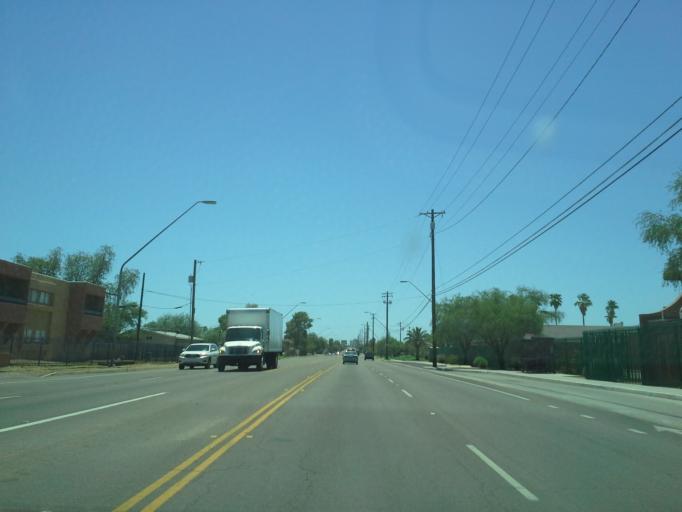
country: US
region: Arizona
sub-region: Pima County
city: Flowing Wells
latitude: 32.2695
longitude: -110.9720
